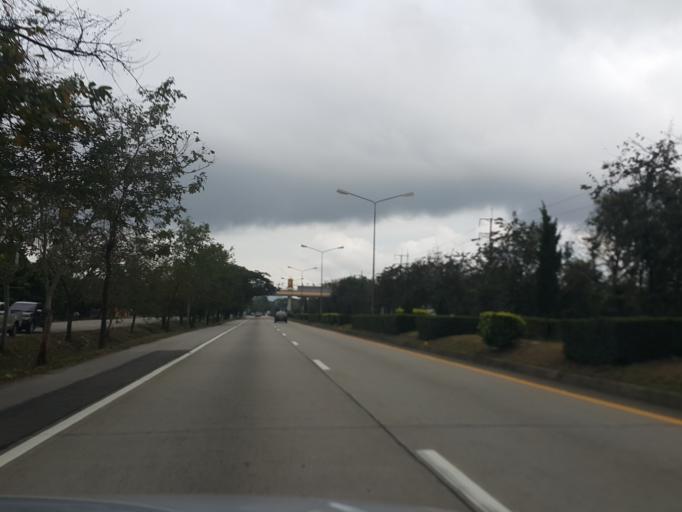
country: TH
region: Lampang
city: Lampang
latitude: 18.2744
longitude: 99.4583
